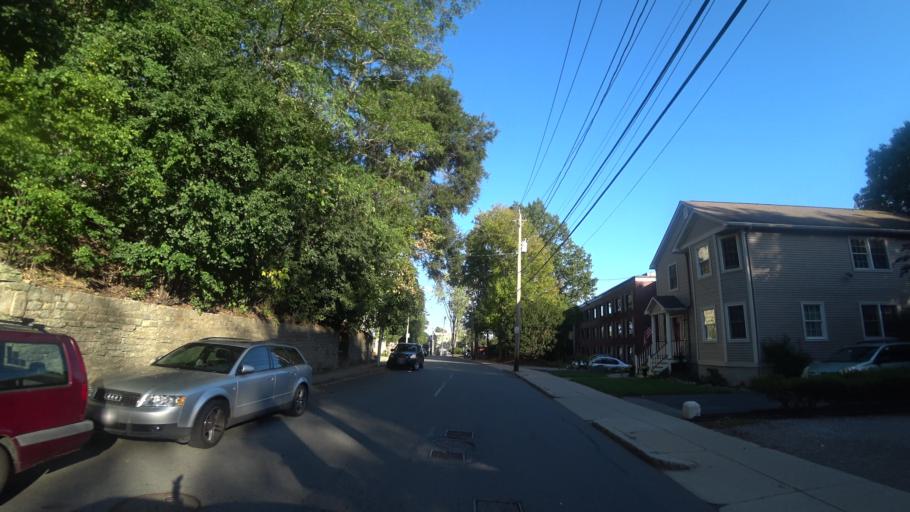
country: US
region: Massachusetts
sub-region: Norfolk County
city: Brookline
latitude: 42.3281
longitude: -71.1061
